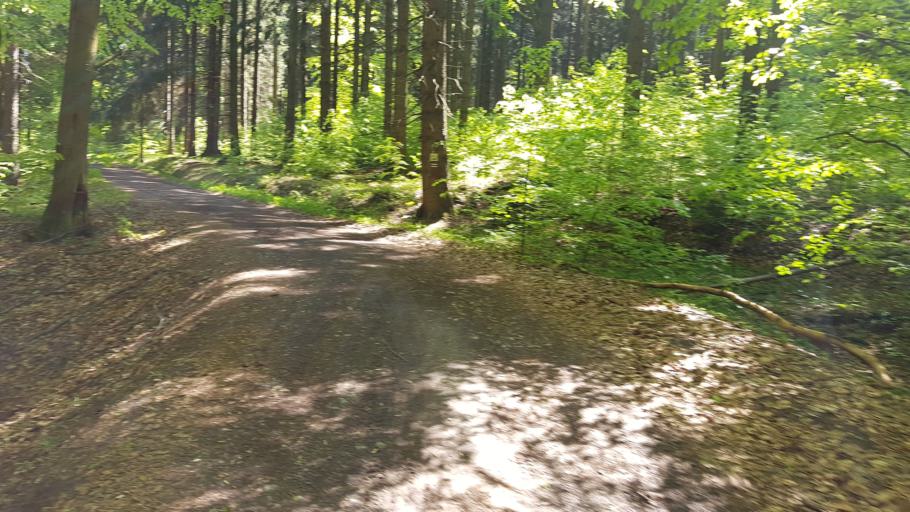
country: PL
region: Lower Silesian Voivodeship
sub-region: Powiat klodzki
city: Radkow
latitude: 50.4718
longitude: 16.3896
